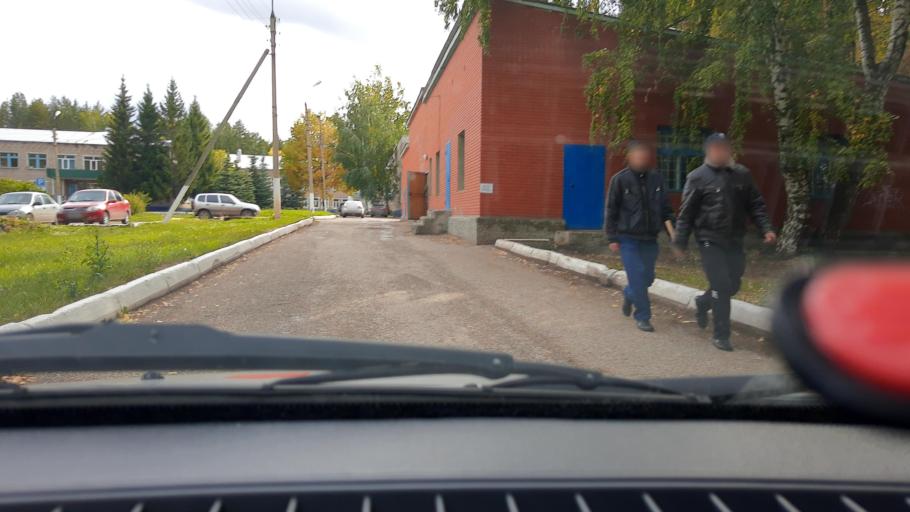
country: RU
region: Bashkortostan
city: Belebey
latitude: 54.1036
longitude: 54.0944
